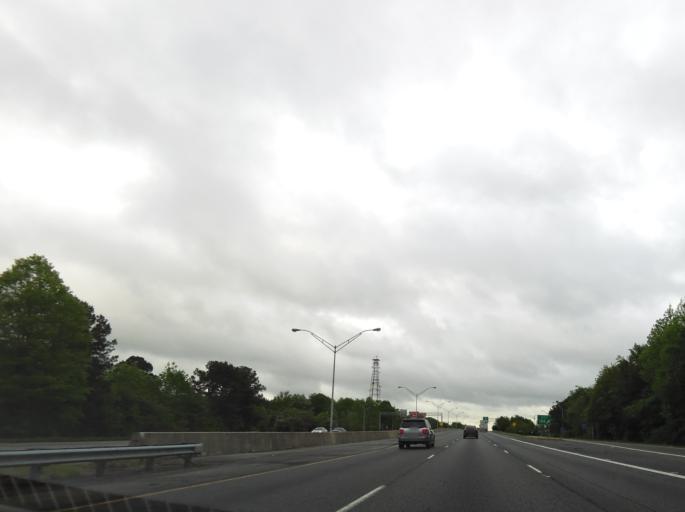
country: US
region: Georgia
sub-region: Monroe County
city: Forsyth
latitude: 33.0559
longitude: -83.9544
